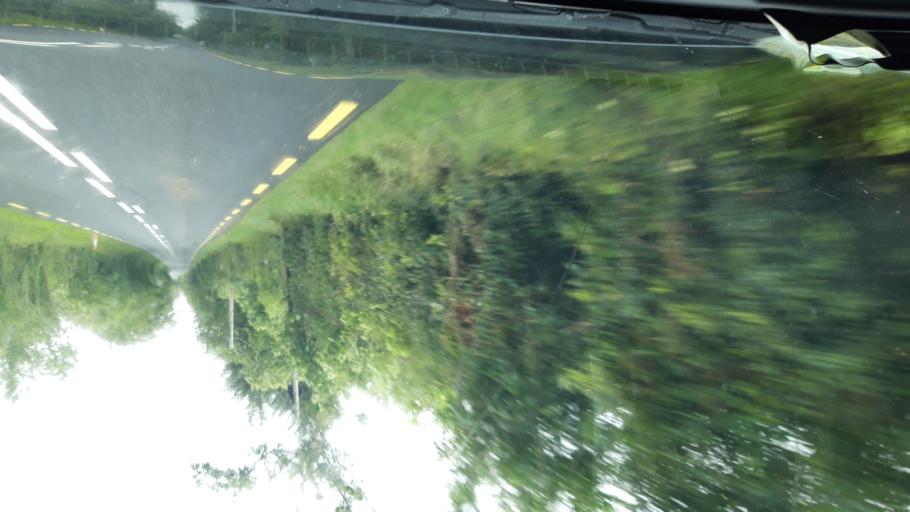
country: IE
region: Leinster
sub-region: Loch Garman
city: New Ross
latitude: 52.4290
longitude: -6.8222
